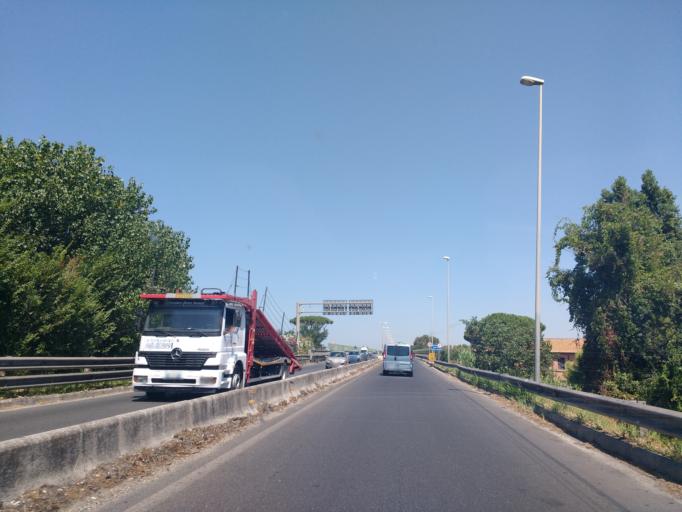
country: IT
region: Latium
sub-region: Citta metropolitana di Roma Capitale
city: Fiumicino-Isola Sacra
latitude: 41.7710
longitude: 12.2581
